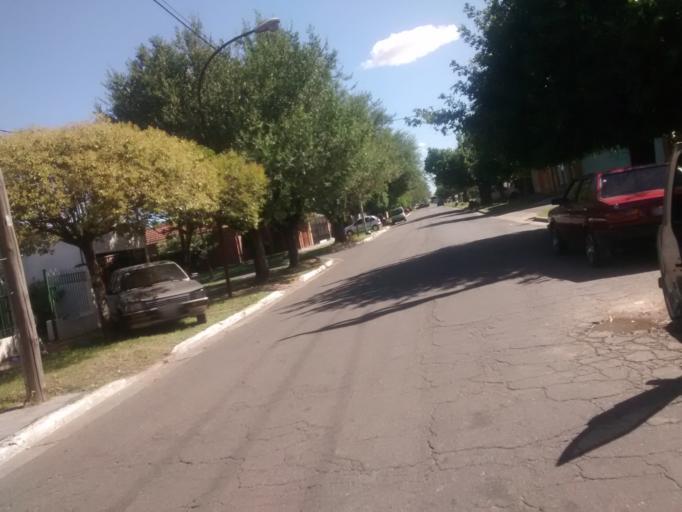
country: AR
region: Buenos Aires
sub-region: Partido de La Plata
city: La Plata
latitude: -34.9308
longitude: -57.9032
